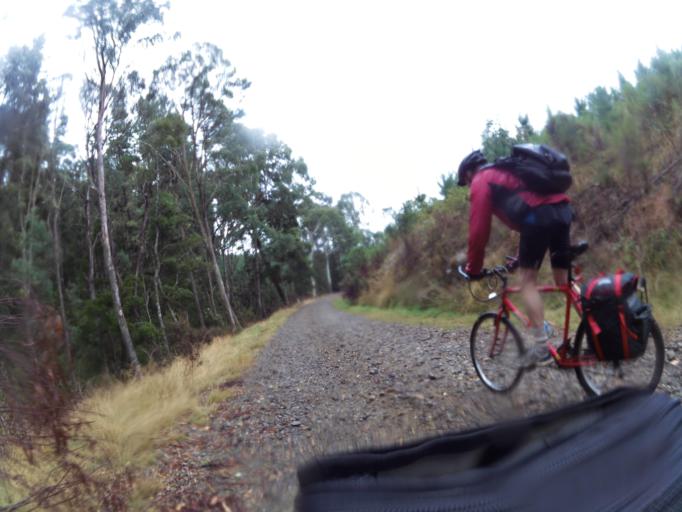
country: AU
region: New South Wales
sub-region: Greater Hume Shire
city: Holbrook
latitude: -36.2154
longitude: 147.5662
